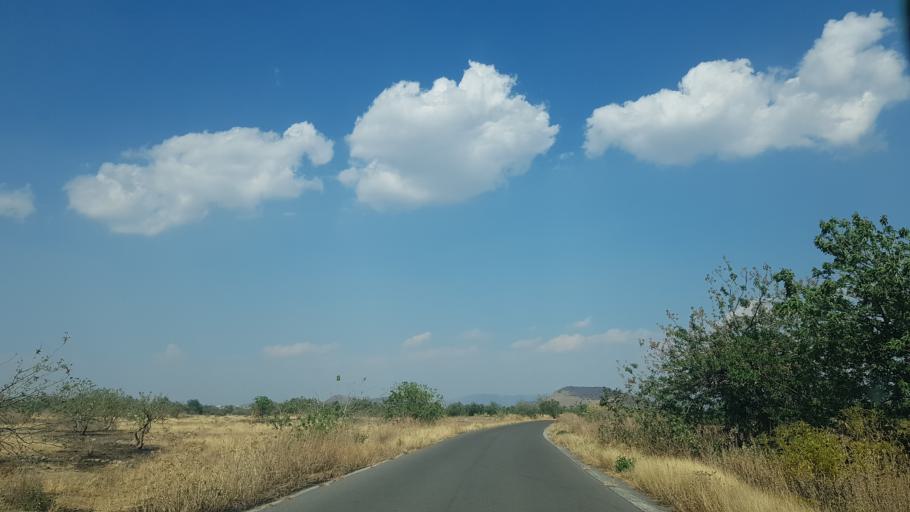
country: MX
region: Puebla
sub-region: Atlixco
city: Colonia Agricola de Ocotepec (Colonia San Jose)
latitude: 18.9232
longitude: -98.5081
